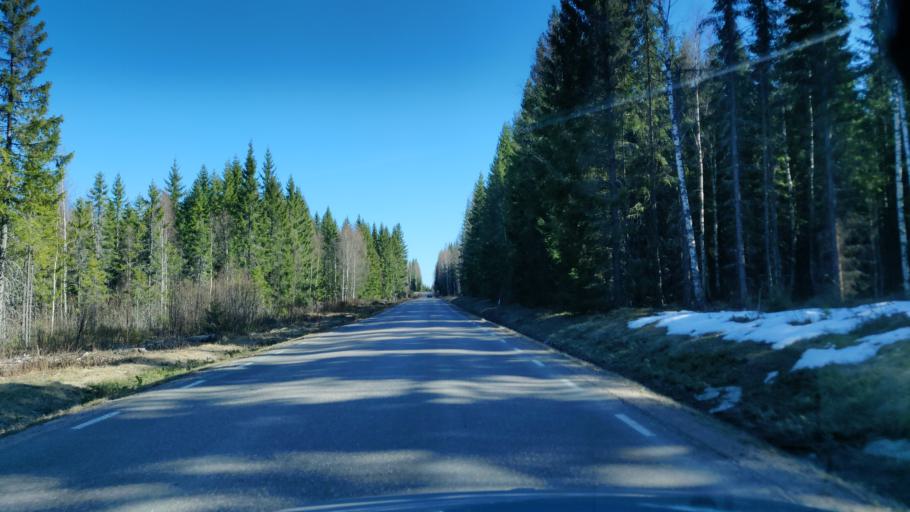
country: SE
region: Vaermland
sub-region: Hagfors Kommun
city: Hagfors
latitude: 59.9814
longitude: 13.6120
